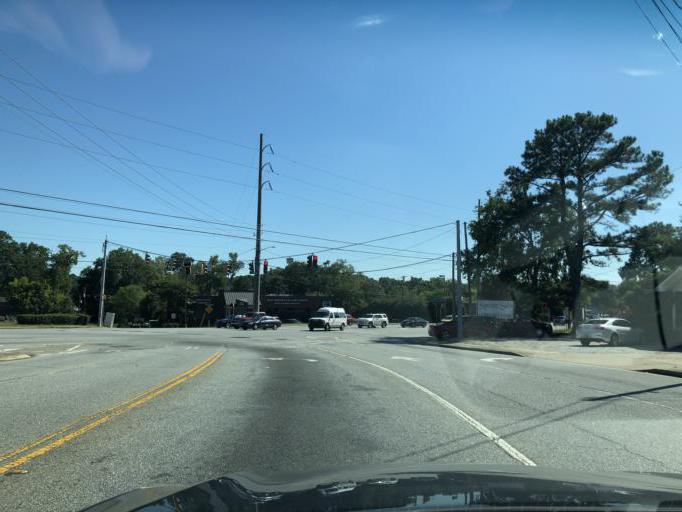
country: US
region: Georgia
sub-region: Muscogee County
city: Columbus
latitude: 32.5028
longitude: -84.9532
